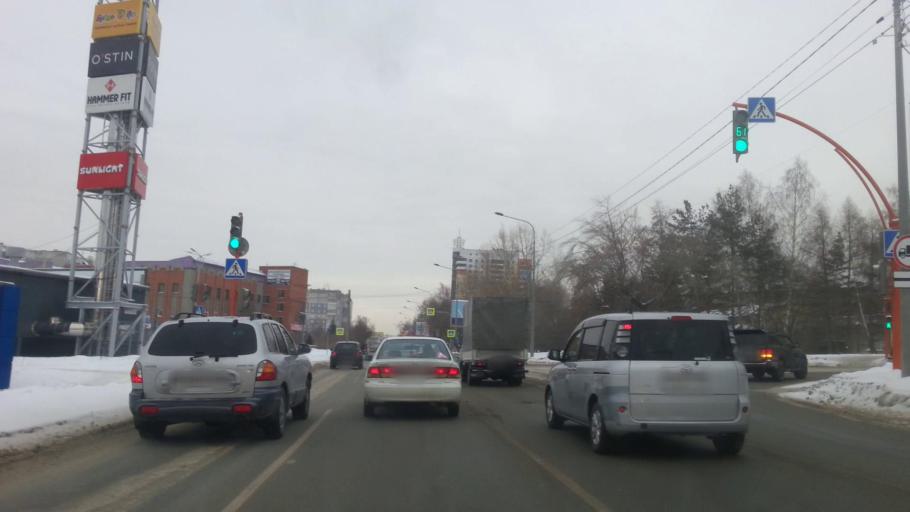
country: RU
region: Altai Krai
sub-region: Gorod Barnaulskiy
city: Barnaul
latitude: 53.3432
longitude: 83.7552
